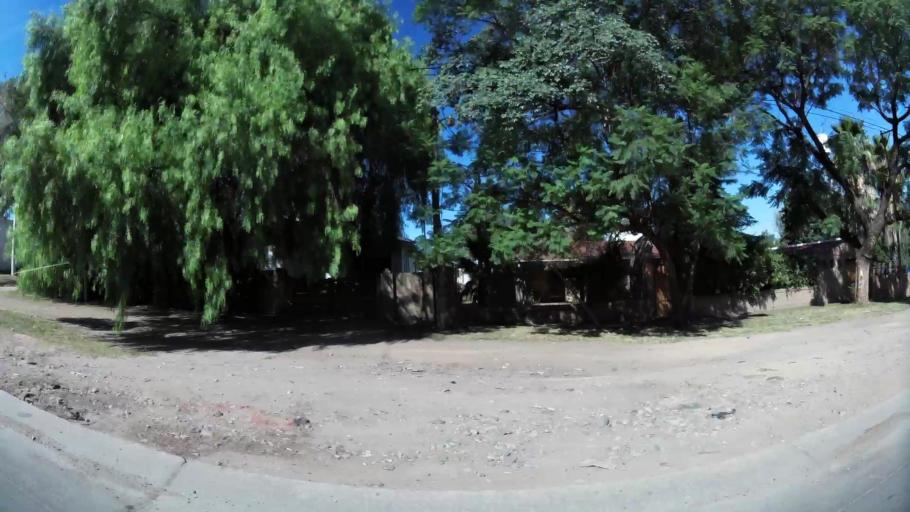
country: AR
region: Cordoba
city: Villa Allende
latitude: -31.3147
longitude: -64.2882
